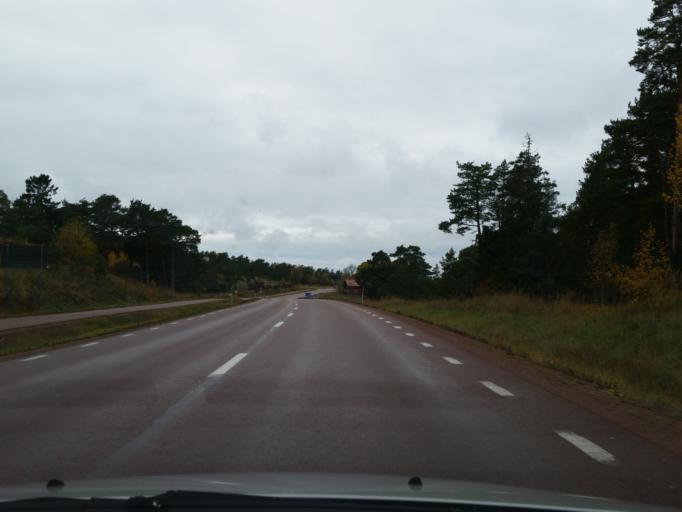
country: AX
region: Alands landsbygd
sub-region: Lumparland
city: Lumparland
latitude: 60.0765
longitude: 20.1945
